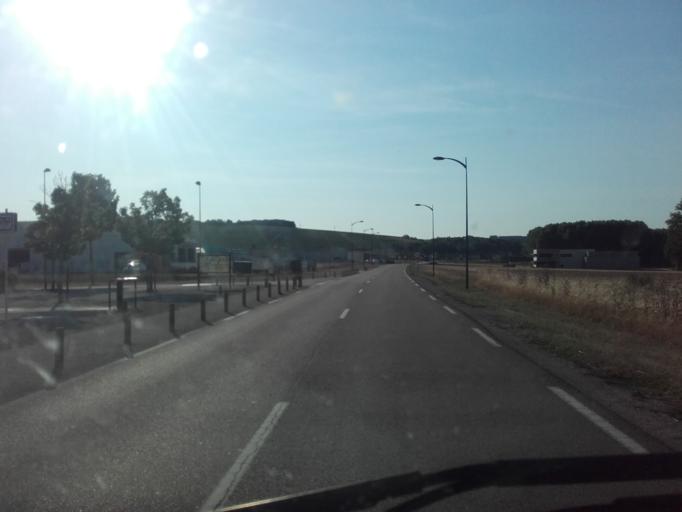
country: FR
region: Bourgogne
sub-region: Departement de l'Yonne
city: Chablis
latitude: 47.8173
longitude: 3.7848
